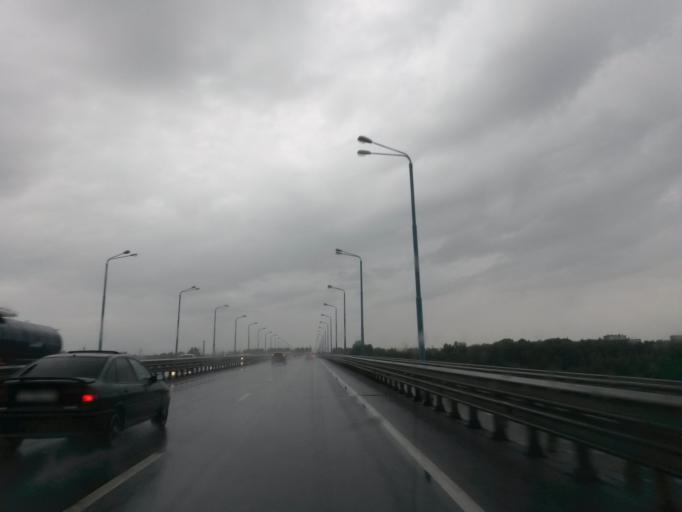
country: RU
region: Jaroslavl
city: Yaroslavl
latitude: 57.6747
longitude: 39.8562
